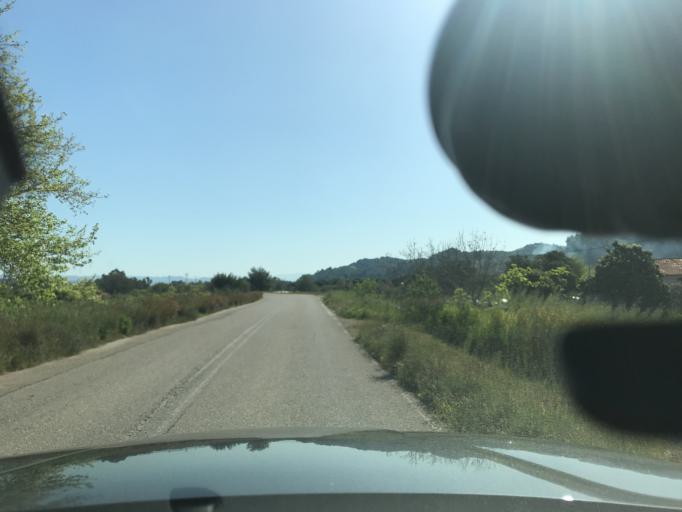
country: GR
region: West Greece
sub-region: Nomos Ileias
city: Epitalion
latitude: 37.6402
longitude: 21.4909
